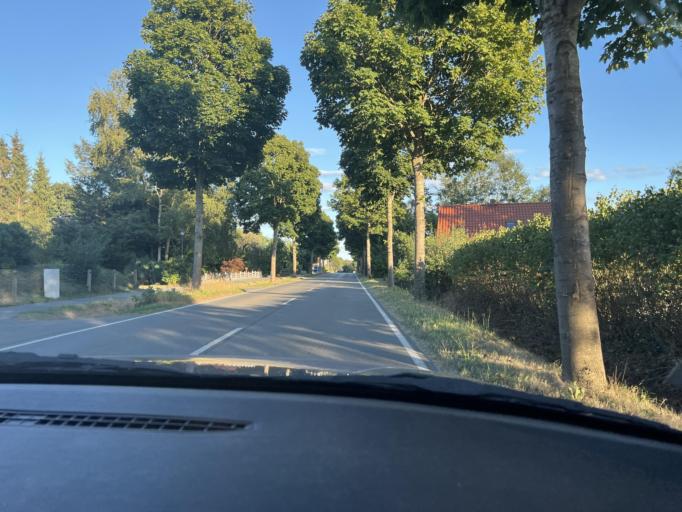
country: DE
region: Schleswig-Holstein
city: Hennstedt
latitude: 54.2855
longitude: 9.1568
